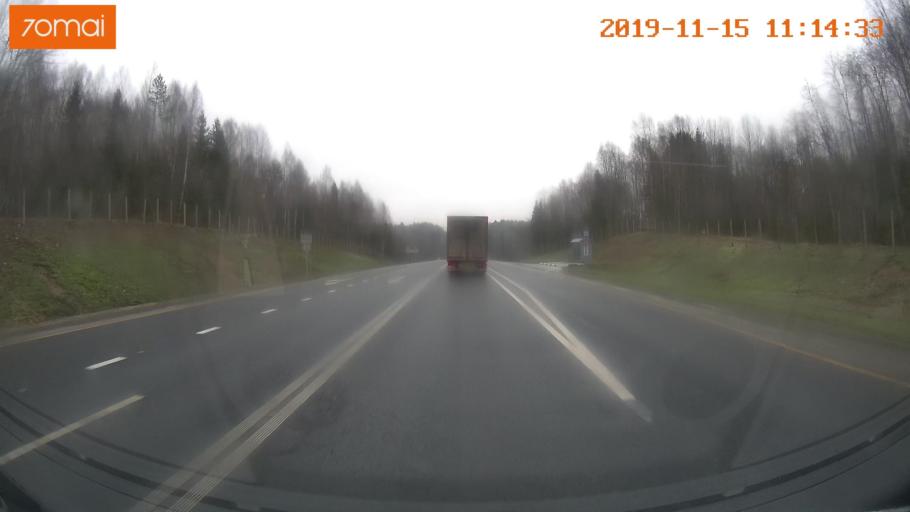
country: RU
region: Vologda
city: Chebsara
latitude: 59.1251
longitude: 39.1906
